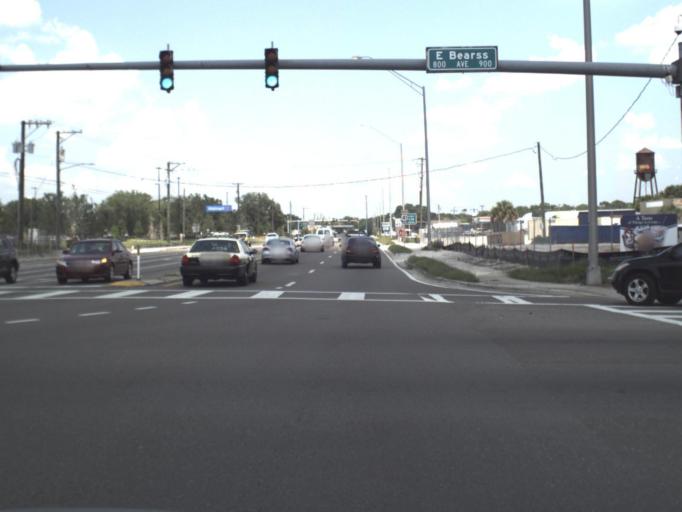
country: US
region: Florida
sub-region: Hillsborough County
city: University
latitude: 28.0879
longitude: -82.4514
